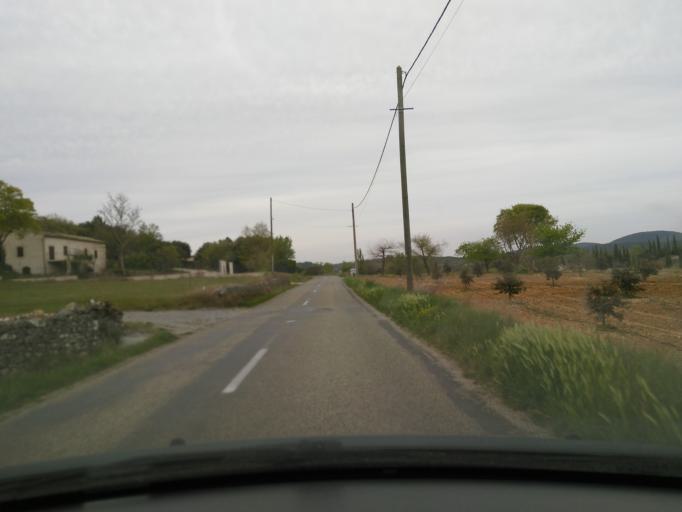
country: FR
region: Rhone-Alpes
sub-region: Departement de l'Ardeche
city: Ruoms
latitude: 44.4267
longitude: 4.4153
